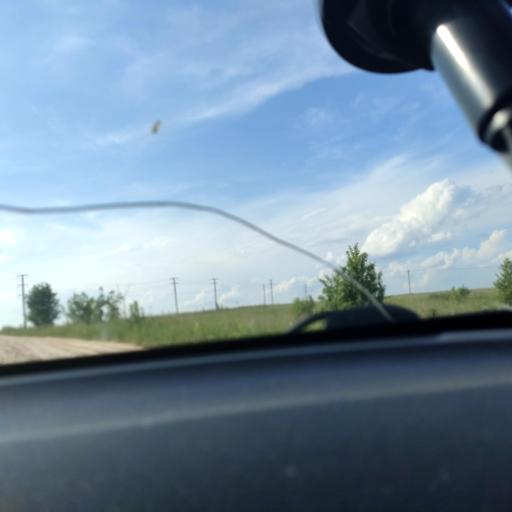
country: RU
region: Tatarstan
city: Verkhniy Uslon
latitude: 55.6477
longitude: 48.9407
